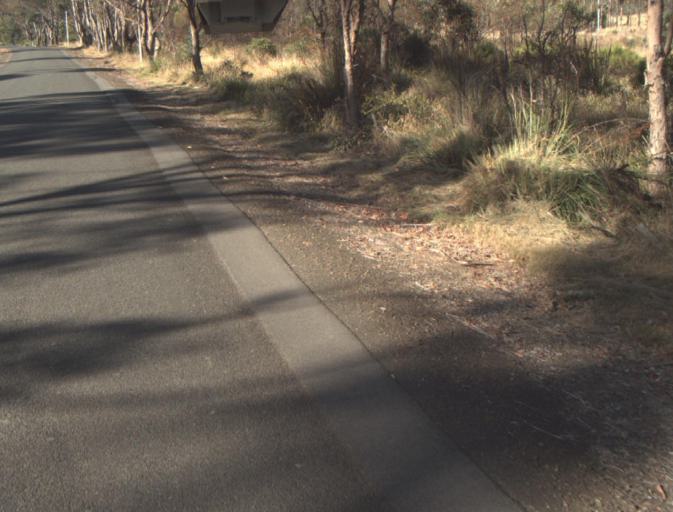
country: AU
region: Tasmania
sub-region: Launceston
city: Newstead
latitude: -41.3844
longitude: 147.2971
